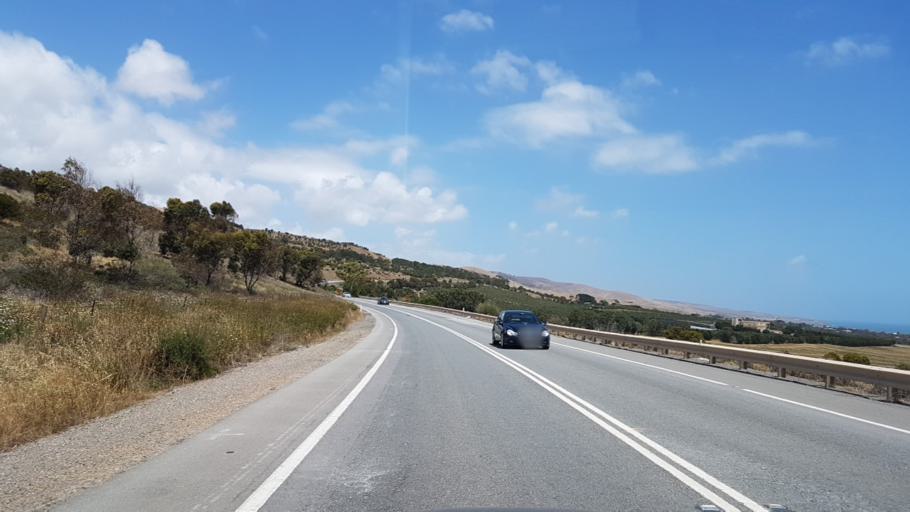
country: AU
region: South Australia
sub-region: Onkaparinga
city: Aldinga
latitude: -35.3310
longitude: 138.4713
